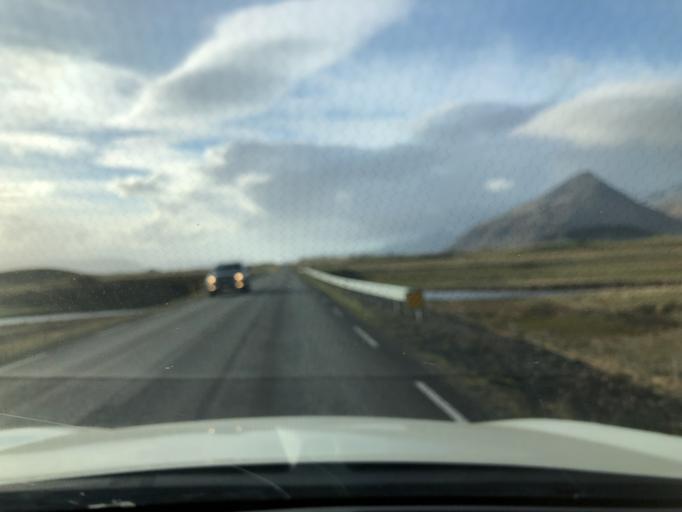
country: IS
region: East
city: Hoefn
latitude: 64.2969
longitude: -15.1940
